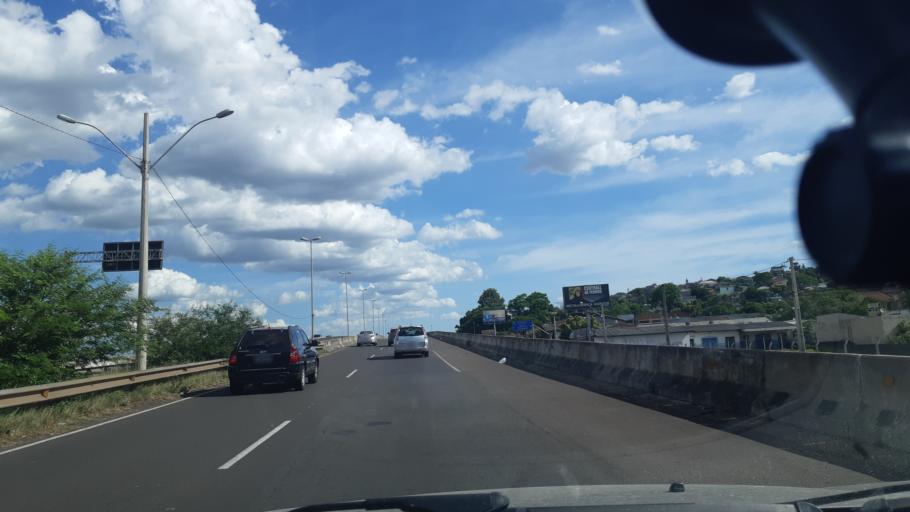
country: BR
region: Rio Grande do Sul
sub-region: Novo Hamburgo
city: Novo Hamburgo
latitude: -29.6674
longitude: -51.1434
